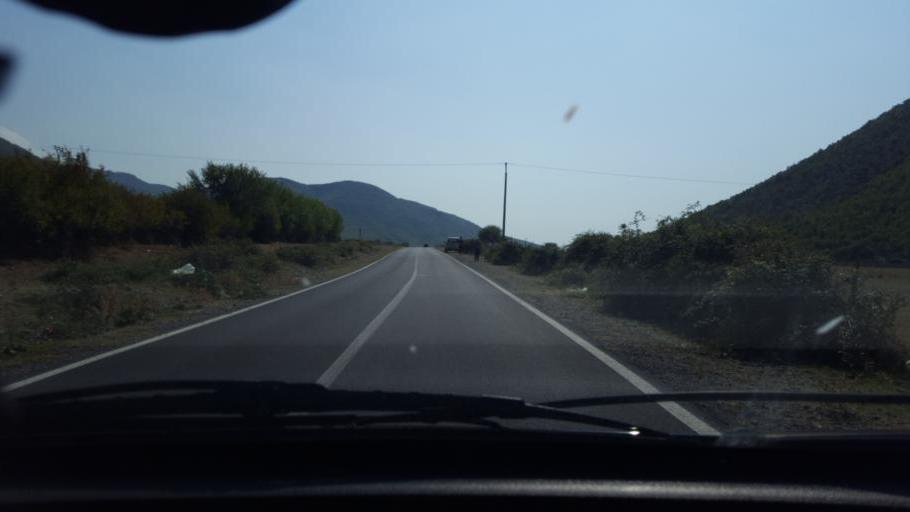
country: AL
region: Shkoder
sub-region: Rrethi i Malesia e Madhe
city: Kastrat
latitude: 42.3949
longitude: 19.4931
